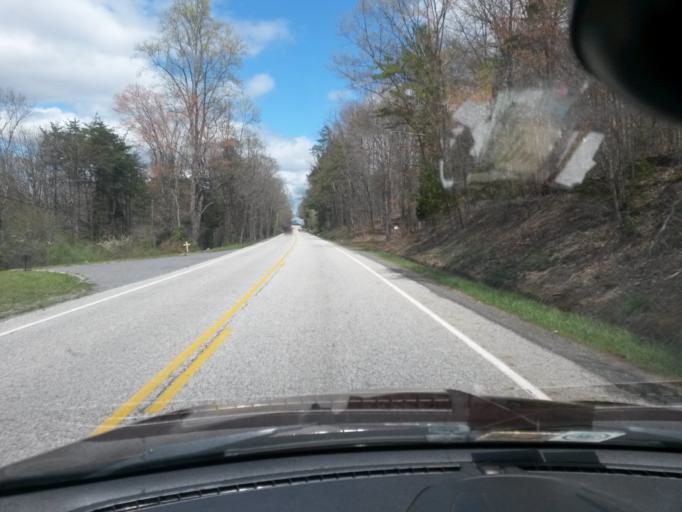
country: US
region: Virginia
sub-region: City of Buena Vista
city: Buena Vista
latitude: 37.6926
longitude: -79.3924
